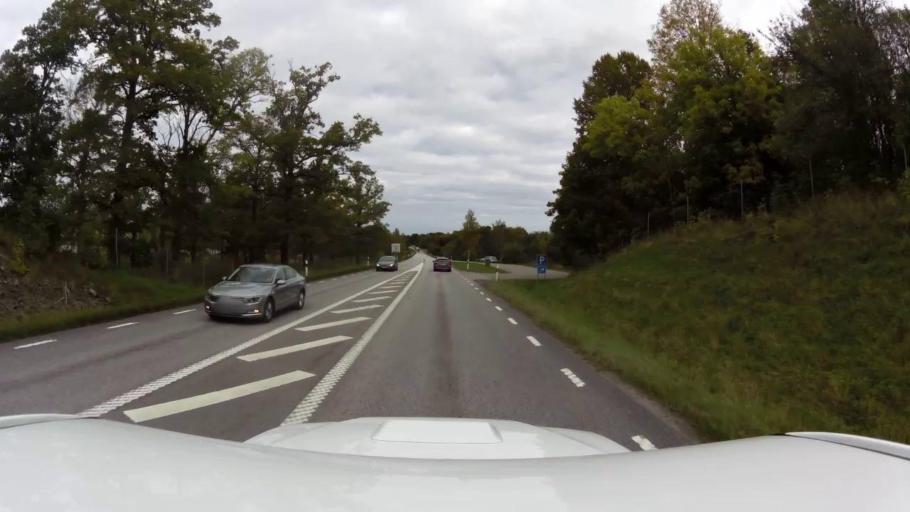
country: SE
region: OEstergoetland
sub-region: Kinda Kommun
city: Rimforsa
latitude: 58.2136
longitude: 15.6673
